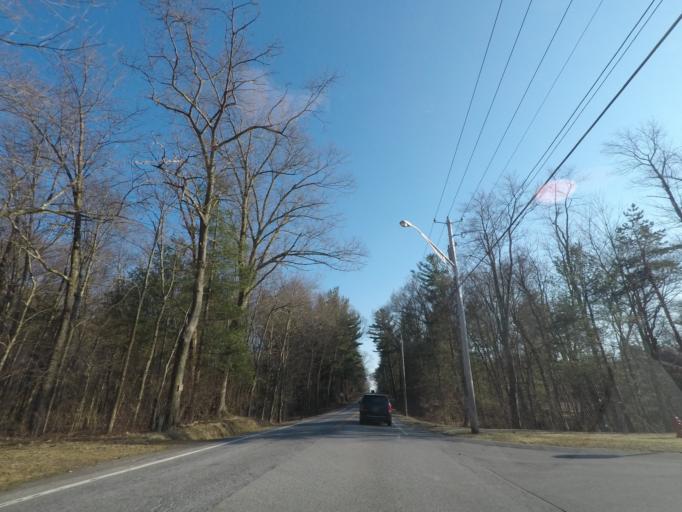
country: US
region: New York
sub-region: Schenectady County
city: Niskayuna
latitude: 42.8270
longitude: -73.7756
